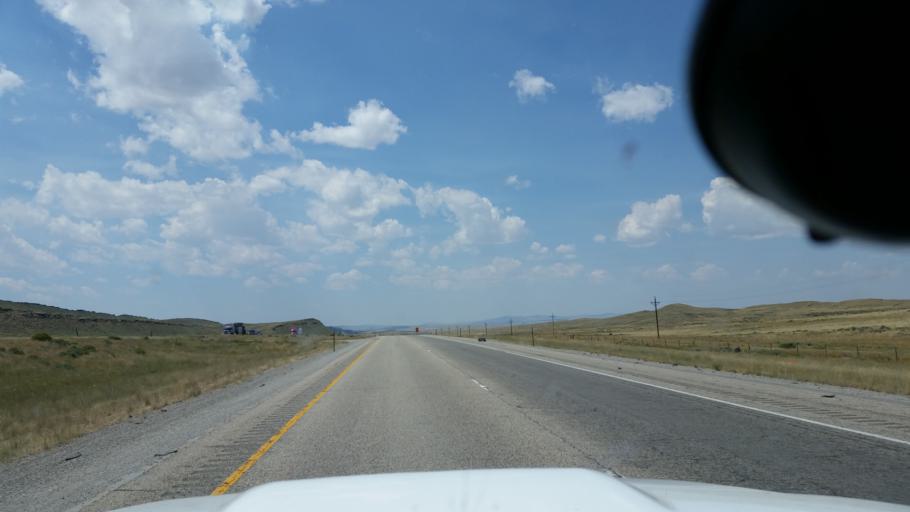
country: US
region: Wyoming
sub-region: Carbon County
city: Saratoga
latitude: 41.7432
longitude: -106.8745
